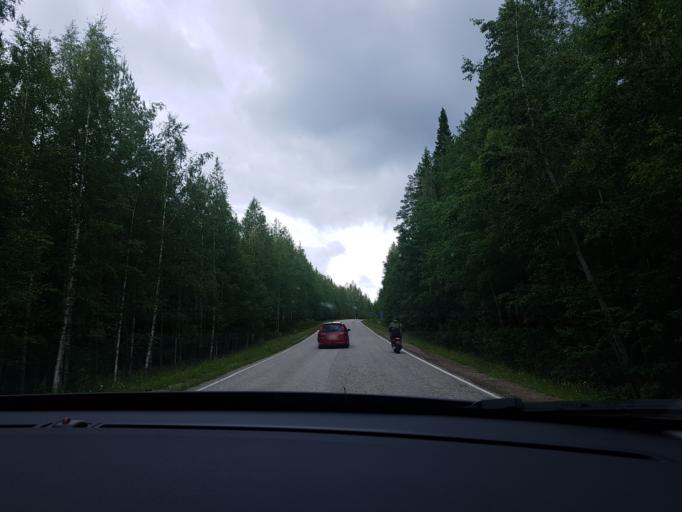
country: FI
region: Kainuu
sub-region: Kehys-Kainuu
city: Kuhmo
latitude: 64.2835
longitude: 29.3783
